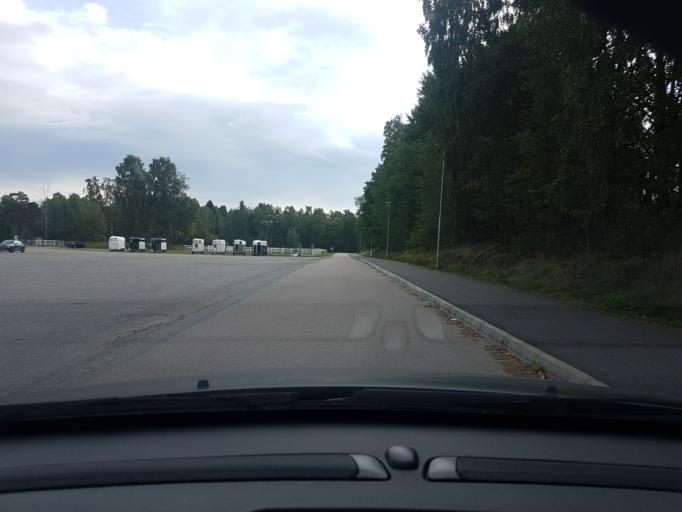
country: SE
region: Vaestra Goetaland
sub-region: Ale Kommun
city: Surte
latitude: 57.8529
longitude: 12.0386
